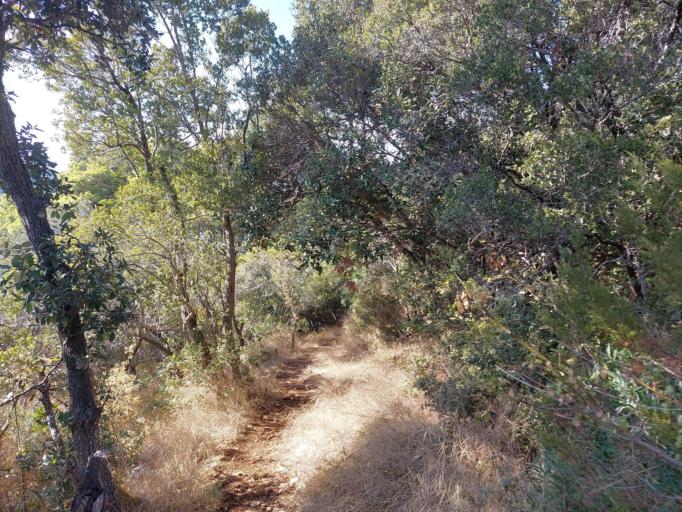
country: HR
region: Dubrovacko-Neretvanska
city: Smokvica
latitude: 42.7654
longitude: 16.8025
